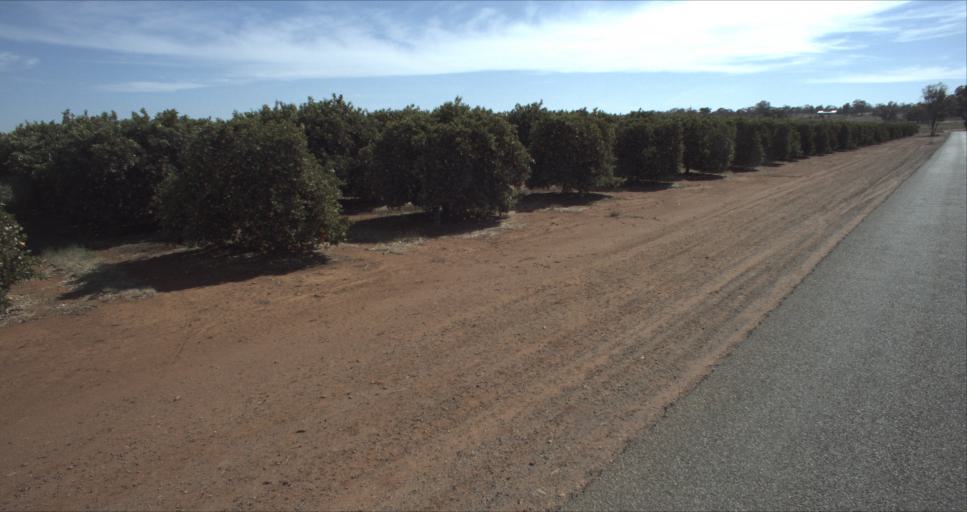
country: AU
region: New South Wales
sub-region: Leeton
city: Leeton
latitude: -34.5874
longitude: 146.4749
